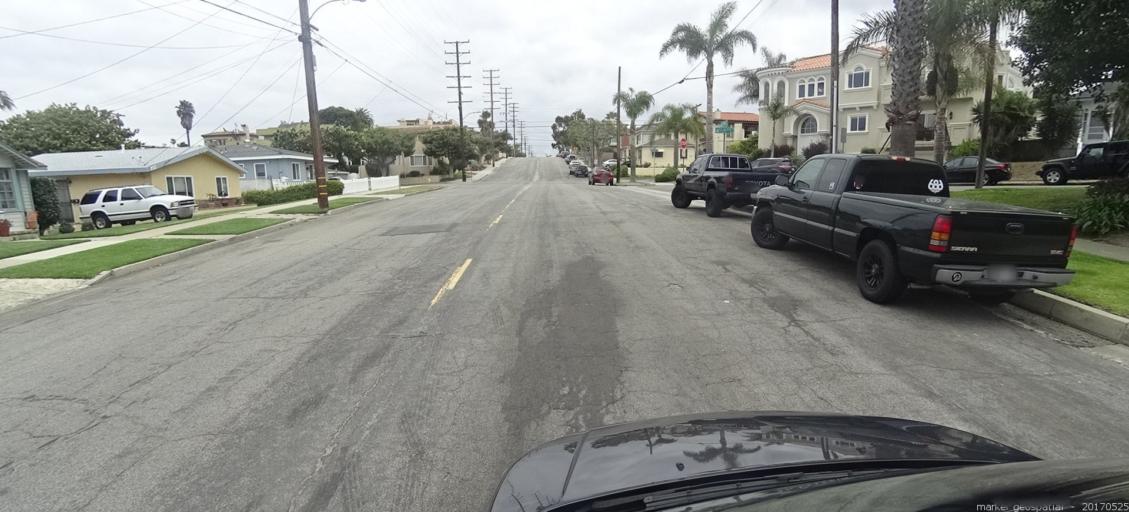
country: US
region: California
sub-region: Los Angeles County
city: Redondo Beach
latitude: 33.8490
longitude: -118.3854
